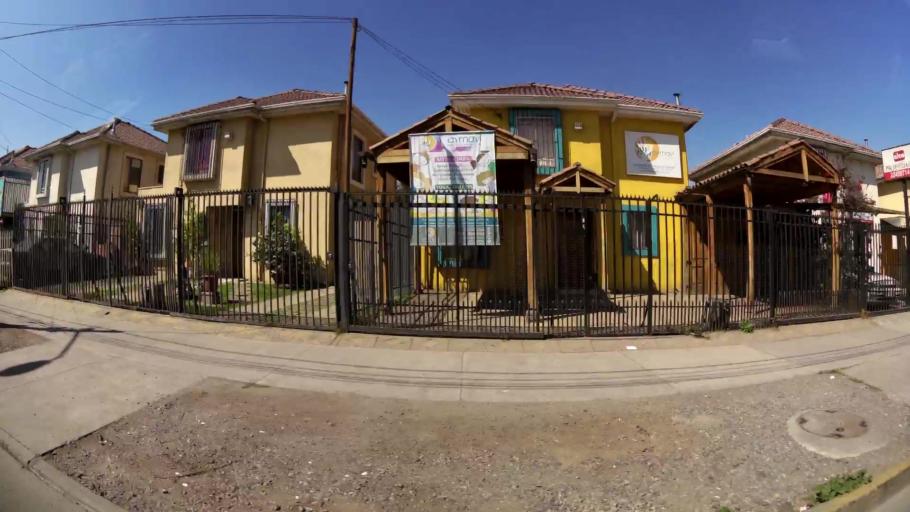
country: CL
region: Santiago Metropolitan
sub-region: Provincia de Santiago
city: Lo Prado
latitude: -33.3539
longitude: -70.7290
